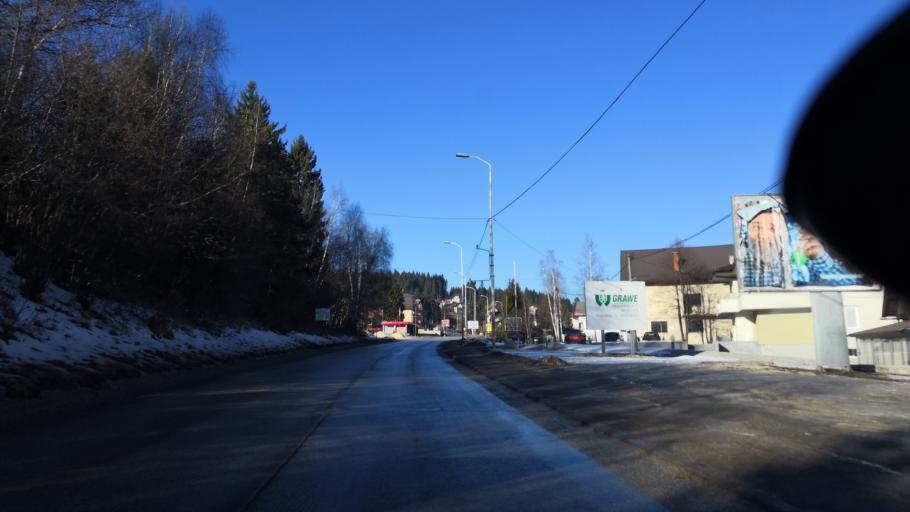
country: BA
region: Republika Srpska
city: Pale
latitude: 43.8202
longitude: 18.5587
